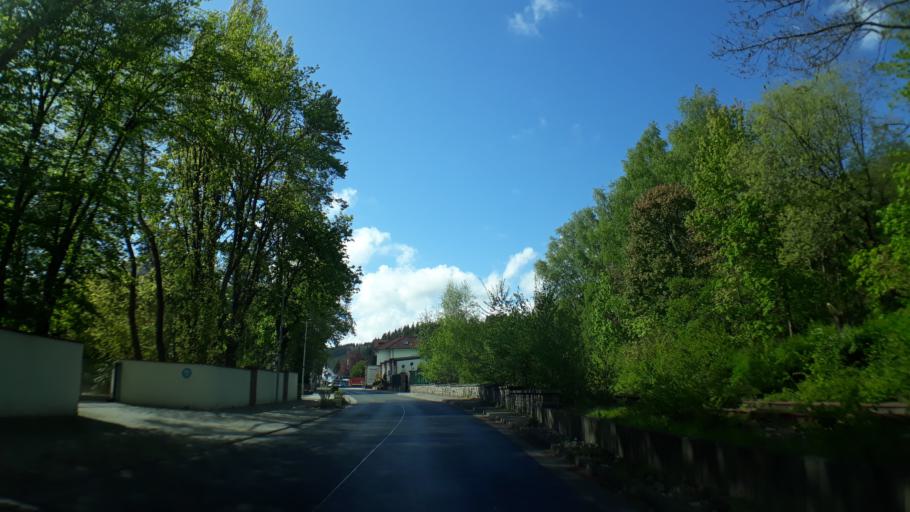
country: DE
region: North Rhine-Westphalia
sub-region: Regierungsbezirk Koln
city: Hellenthal
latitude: 50.4897
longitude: 6.4453
